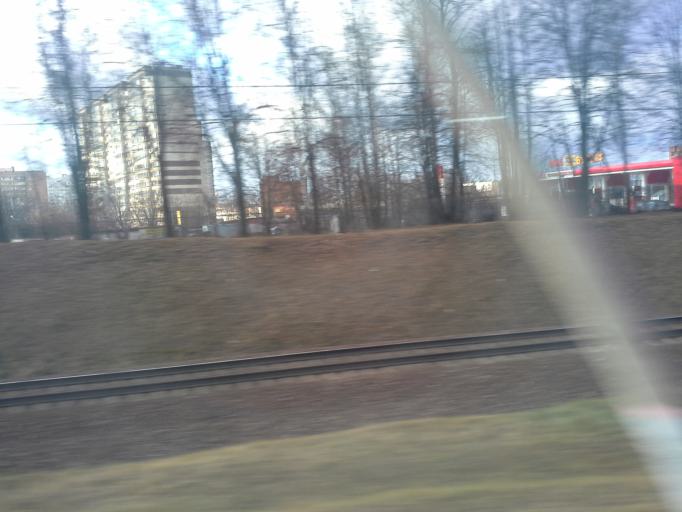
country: RU
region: Moskovskaya
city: Mytishchi
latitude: 55.9248
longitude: 37.7733
